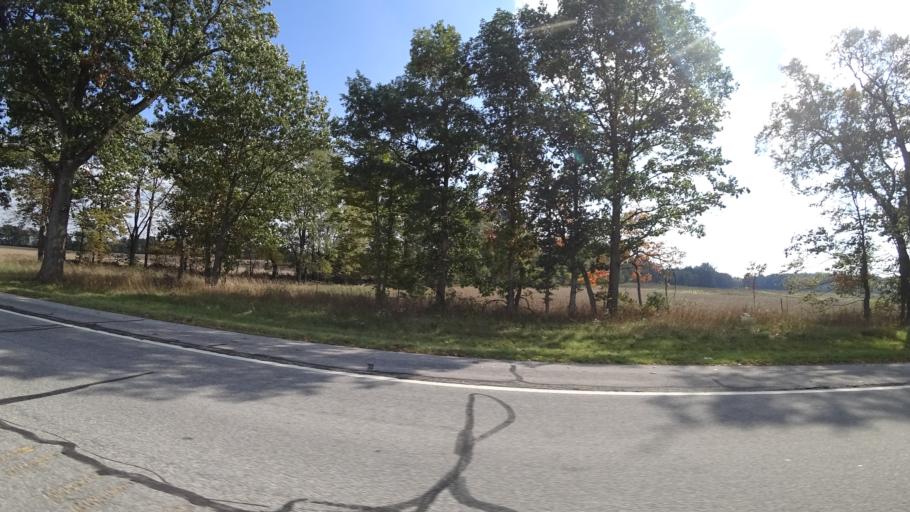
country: US
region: Michigan
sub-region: Calhoun County
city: Athens
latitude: 42.0463
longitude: -85.3035
